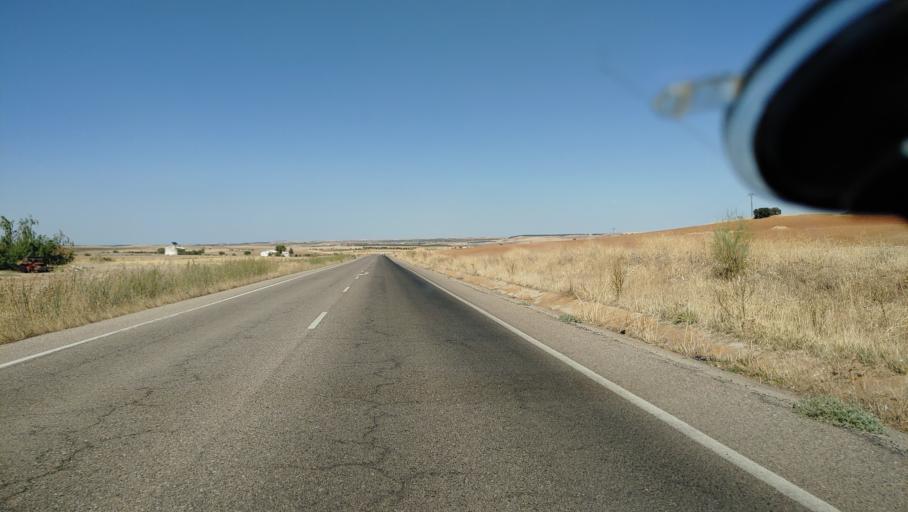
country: ES
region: Castille-La Mancha
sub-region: Province of Toledo
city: Pulgar
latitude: 39.7147
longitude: -4.1305
